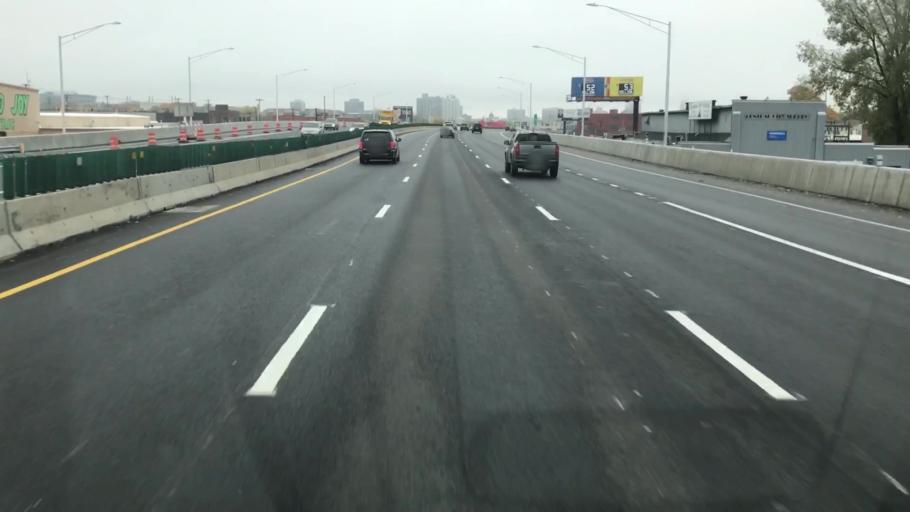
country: US
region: New York
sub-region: Onondaga County
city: Syracuse
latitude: 43.0526
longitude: -76.1248
